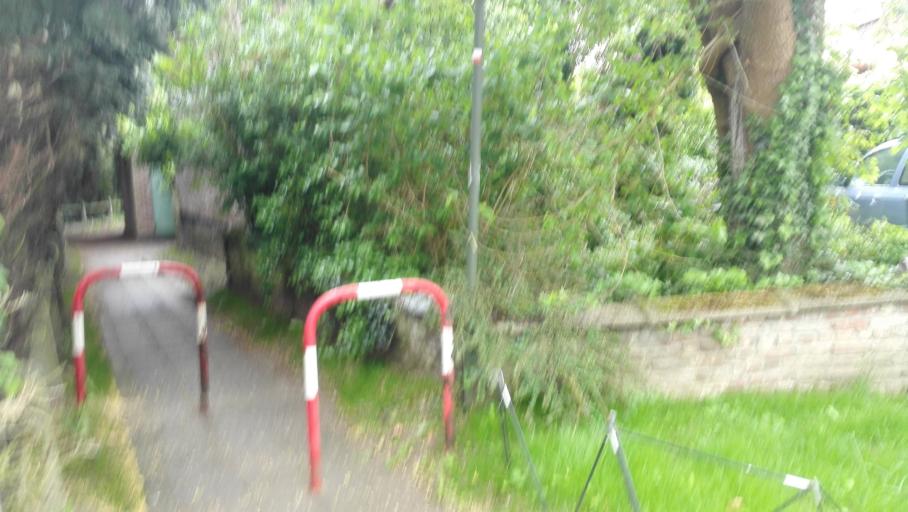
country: BE
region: Flanders
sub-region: Provincie Vlaams-Brabant
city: Leuven
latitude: 50.8959
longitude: 4.7307
